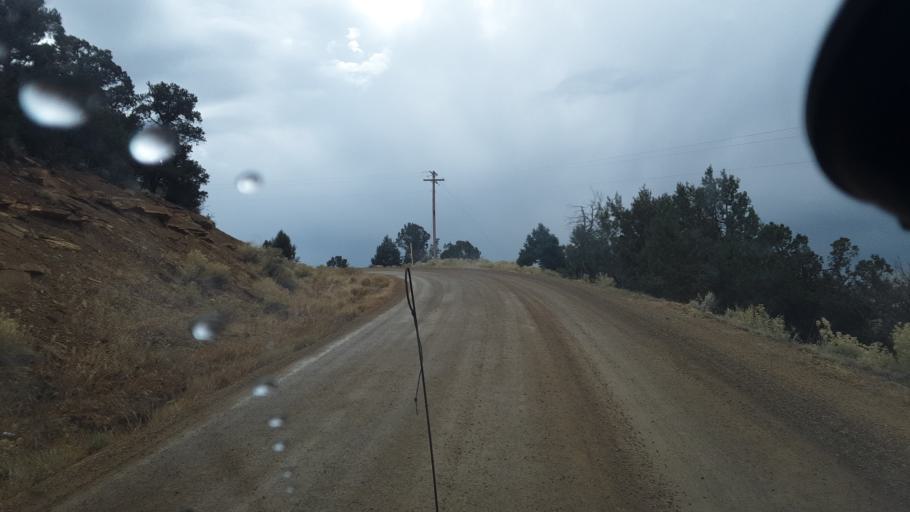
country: US
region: Colorado
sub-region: Montezuma County
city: Mancos
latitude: 37.1991
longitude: -108.1369
